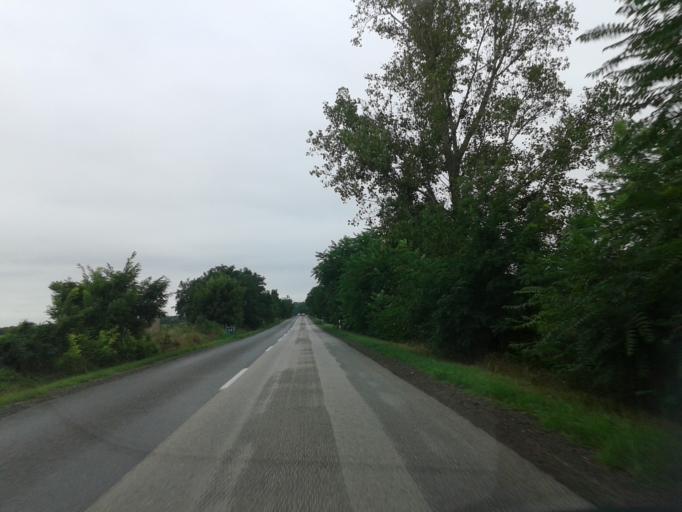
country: HU
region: Bacs-Kiskun
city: Dunavecse
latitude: 46.9429
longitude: 18.9802
